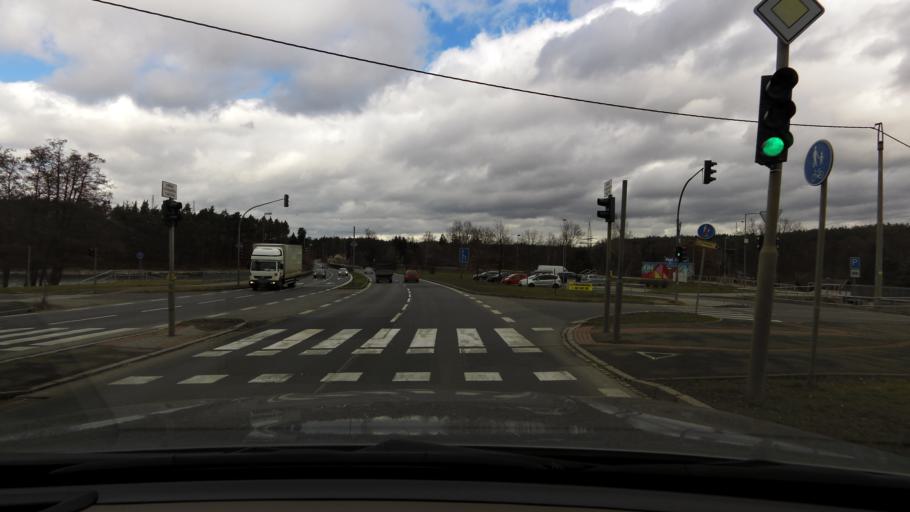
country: CZ
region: Plzensky
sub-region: Okres Plzen-Sever
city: Tremosna
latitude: 49.7852
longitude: 13.3852
